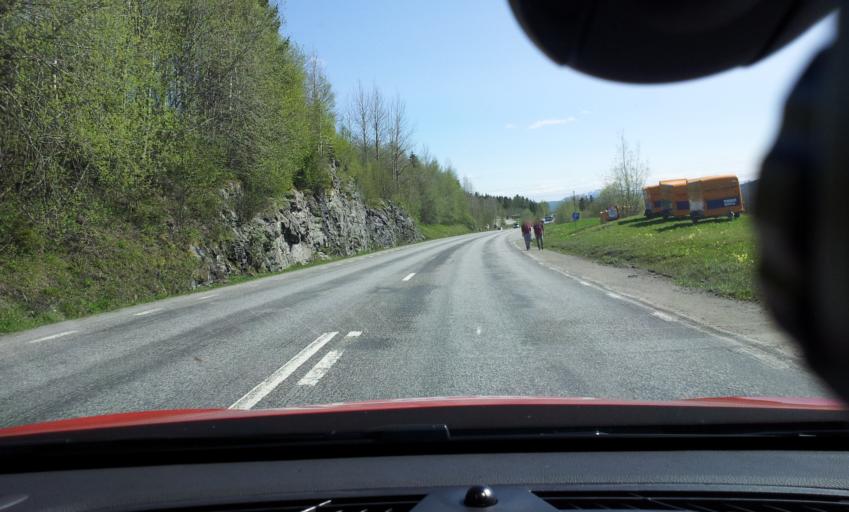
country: SE
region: Jaemtland
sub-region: Are Kommun
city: Are
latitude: 63.3771
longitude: 13.1568
